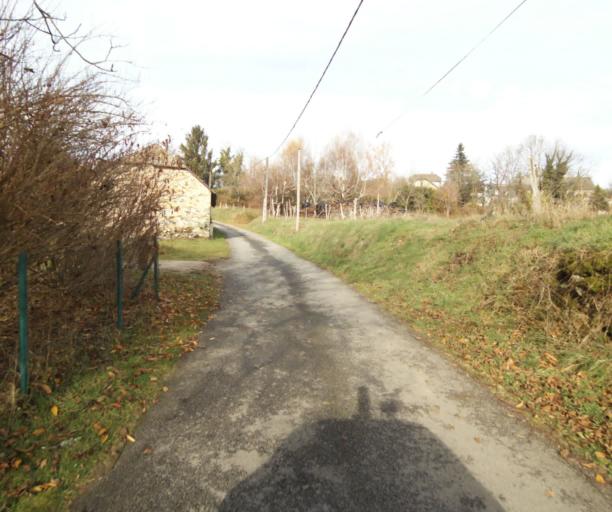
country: FR
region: Limousin
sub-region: Departement de la Correze
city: Beynat
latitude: 45.1696
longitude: 1.7346
